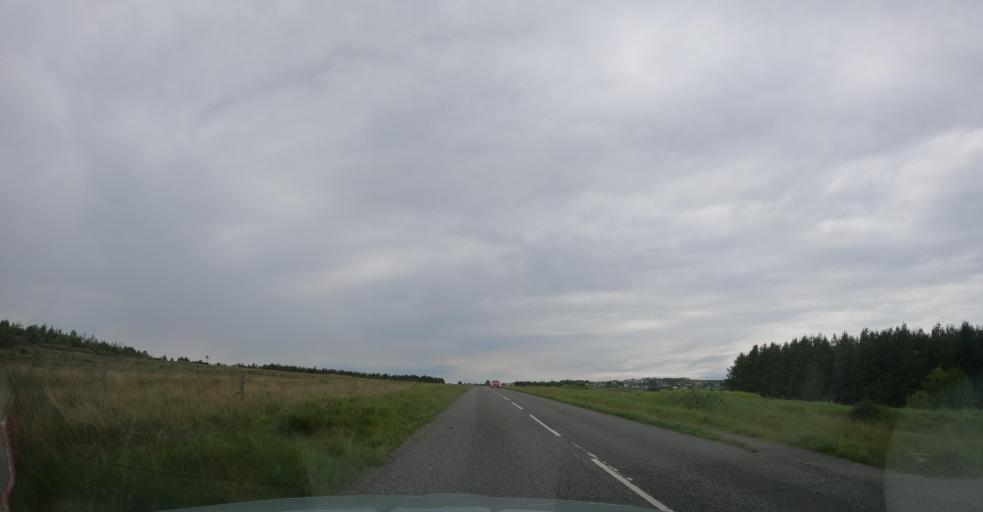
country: GB
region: Scotland
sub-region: Eilean Siar
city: Isle of Lewis
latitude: 58.2429
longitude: -6.3715
